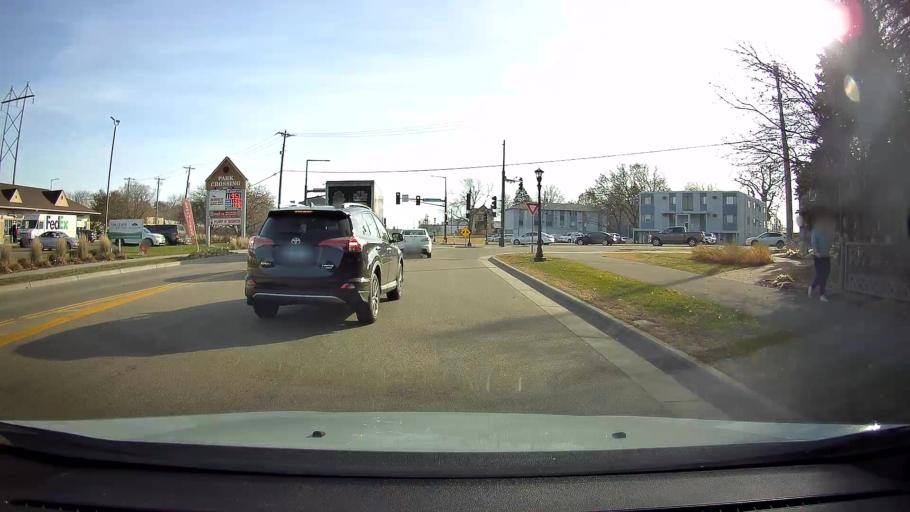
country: US
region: Minnesota
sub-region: Ramsey County
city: Lauderdale
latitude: 44.9743
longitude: -93.1953
